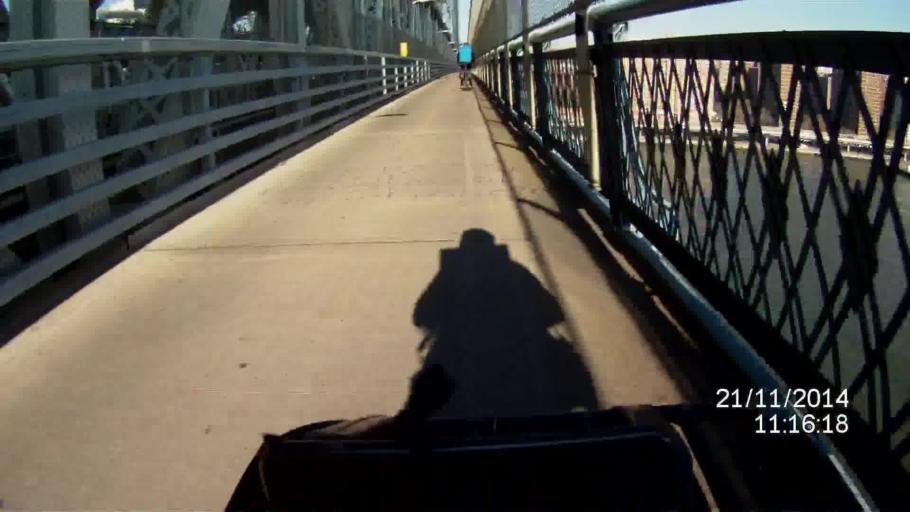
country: US
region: New York
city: New York City
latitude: 40.7074
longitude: -73.9904
